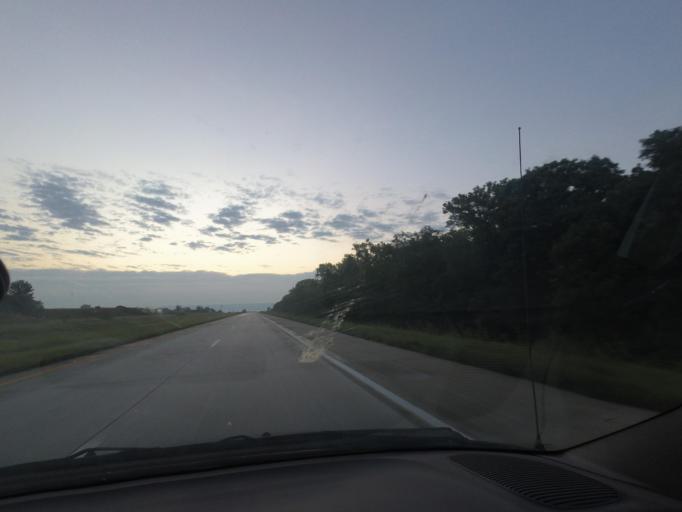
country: US
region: Missouri
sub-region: Macon County
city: Macon
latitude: 39.7586
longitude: -92.6493
